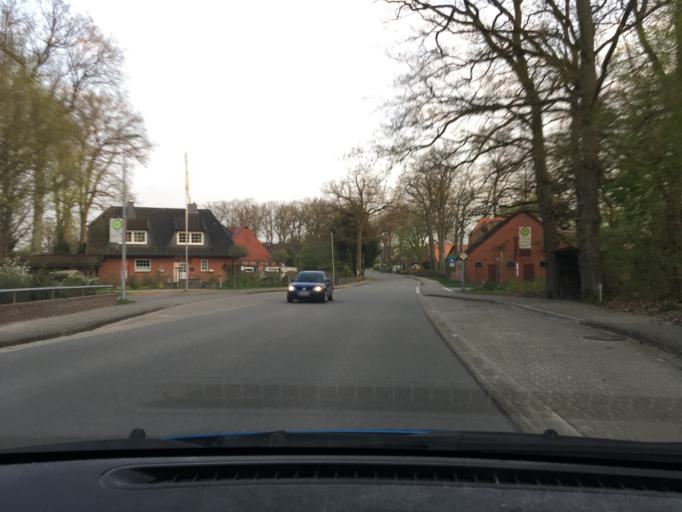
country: DE
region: Lower Saxony
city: Oldendorf
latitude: 53.1558
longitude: 10.2140
